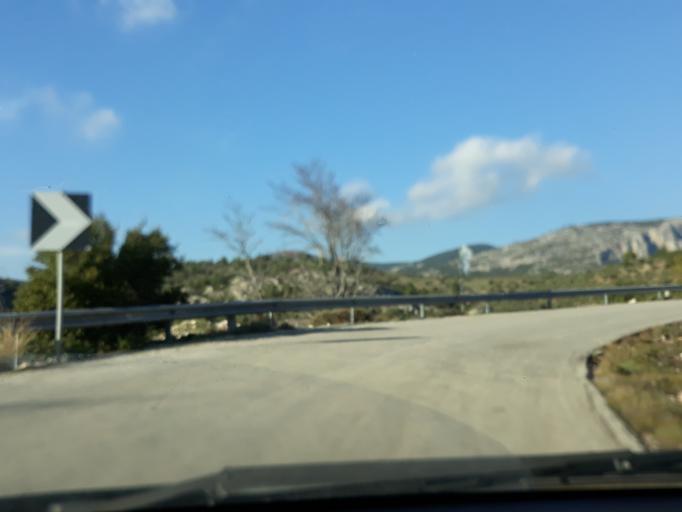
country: GR
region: Attica
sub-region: Nomarchia Dytikis Attikis
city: Fyli
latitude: 38.1166
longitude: 23.6466
